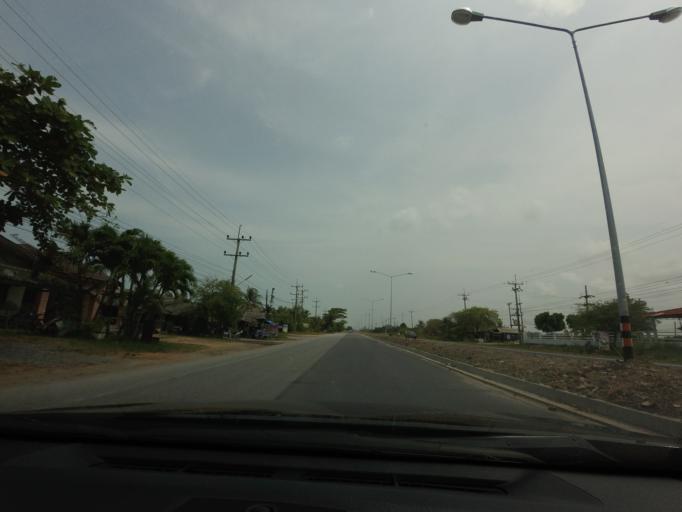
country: TH
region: Songkhla
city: Ranot
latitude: 7.8856
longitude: 100.3439
